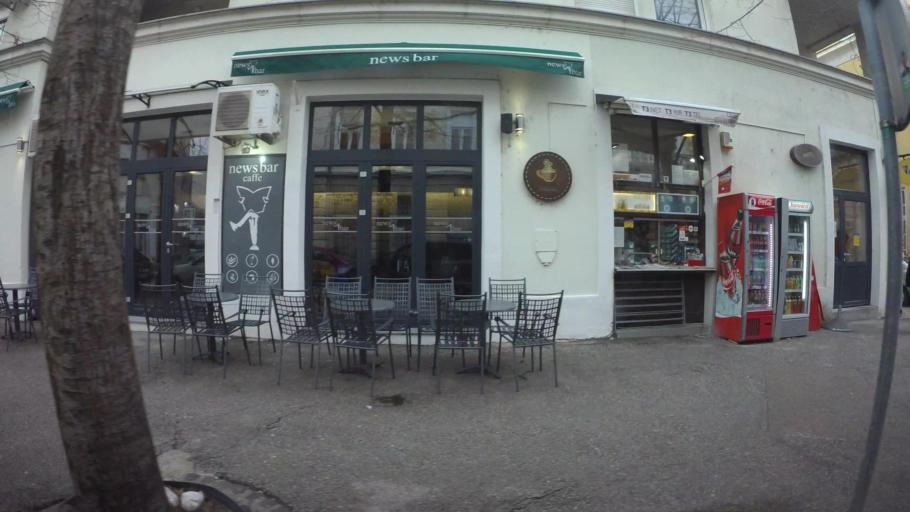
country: BA
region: Federation of Bosnia and Herzegovina
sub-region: Hercegovacko-Bosanski Kanton
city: Mostar
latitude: 43.3428
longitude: 17.8094
